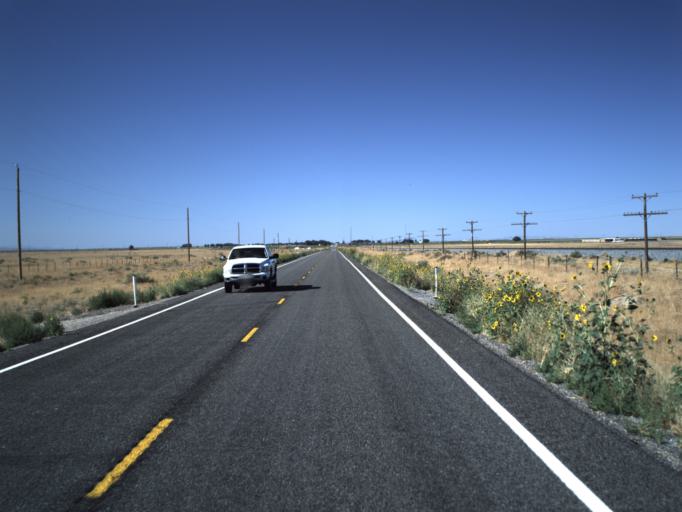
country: US
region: Utah
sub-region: Millard County
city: Delta
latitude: 39.5687
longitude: -112.3447
